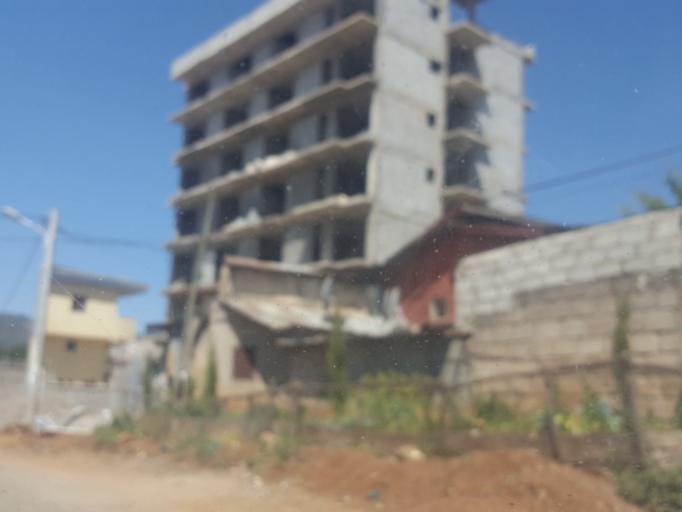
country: ET
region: Adis Abeba
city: Addis Ababa
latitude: 9.0578
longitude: 38.7254
